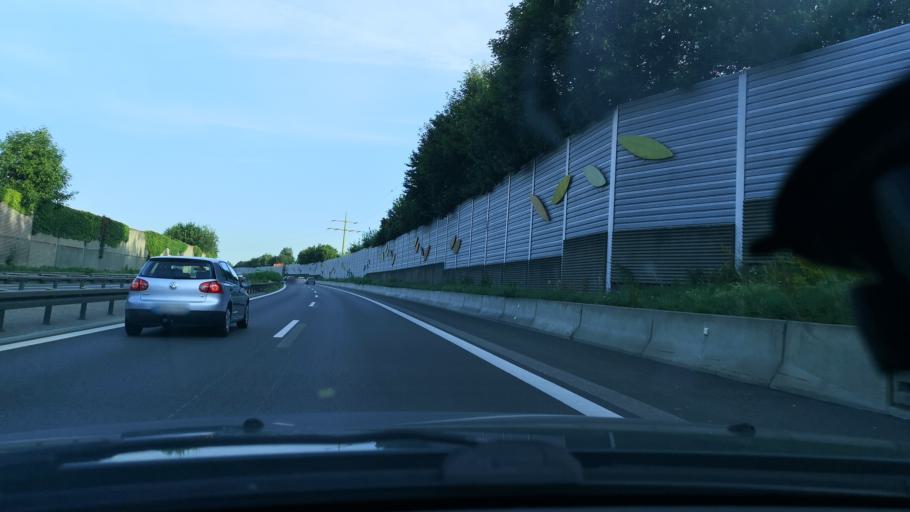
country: DE
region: Baden-Wuerttemberg
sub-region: Regierungsbezirk Stuttgart
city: Eislingen
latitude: 48.6897
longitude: 9.6957
